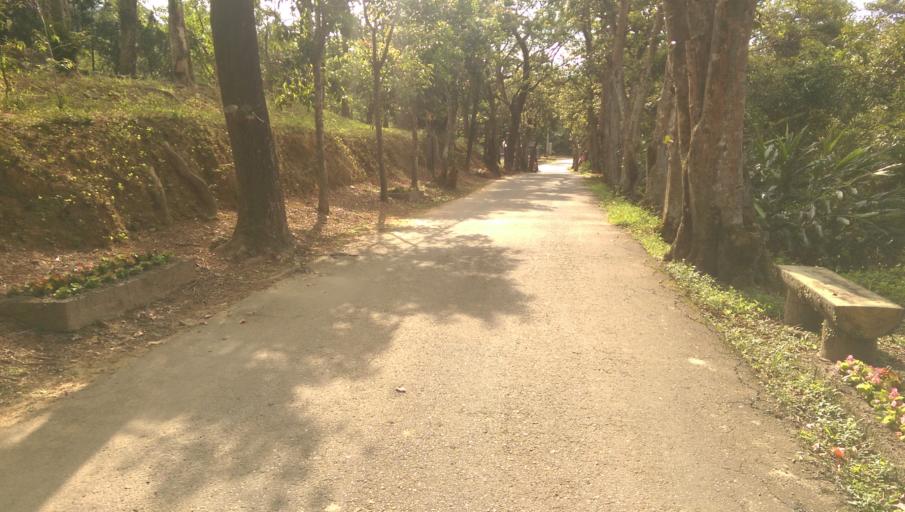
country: TW
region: Taipei
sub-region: Taipei
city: Banqiao
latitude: 24.9317
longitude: 121.5419
